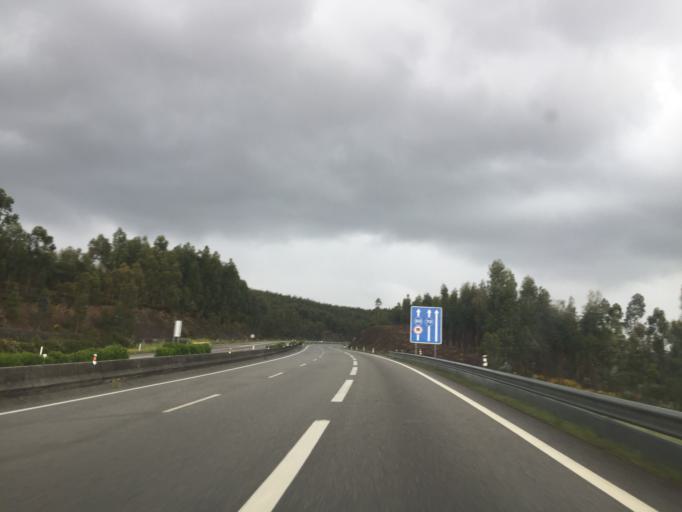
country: PT
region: Aveiro
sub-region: Agueda
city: Valongo
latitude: 40.6612
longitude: -8.3911
